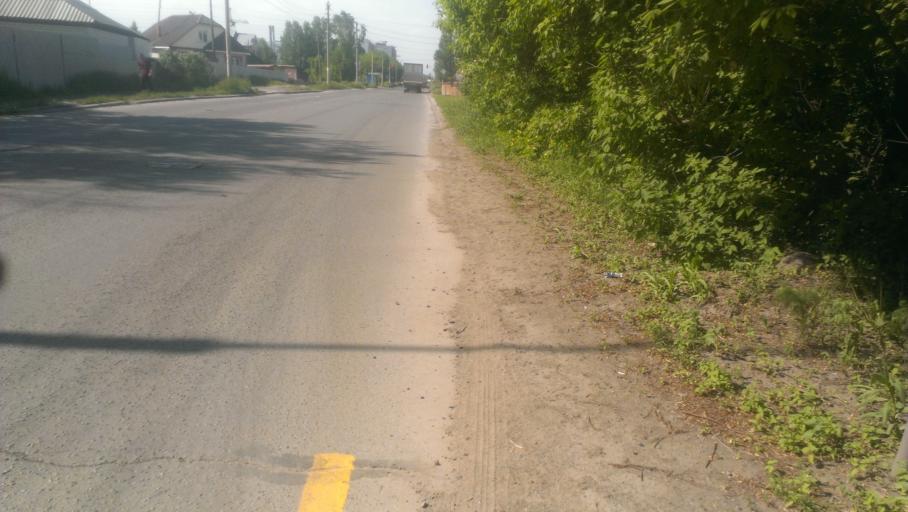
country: RU
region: Altai Krai
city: Novoaltaysk
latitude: 53.4054
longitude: 83.9449
